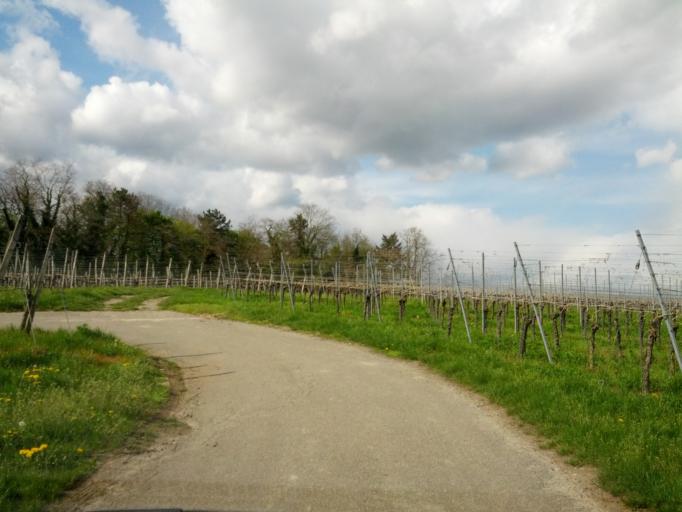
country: DE
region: Baden-Wuerttemberg
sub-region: Freiburg Region
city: Merdingen
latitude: 47.9878
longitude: 7.6819
